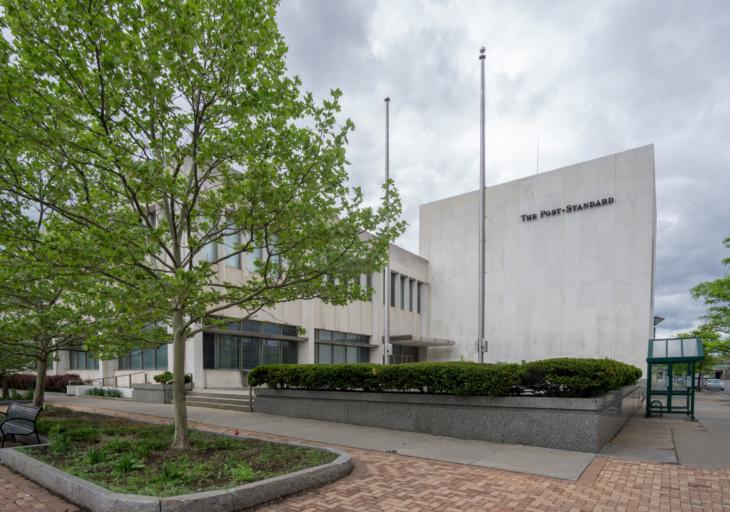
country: US
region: New York
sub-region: Onondaga County
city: Syracuse
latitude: 43.0514
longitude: -76.1522
